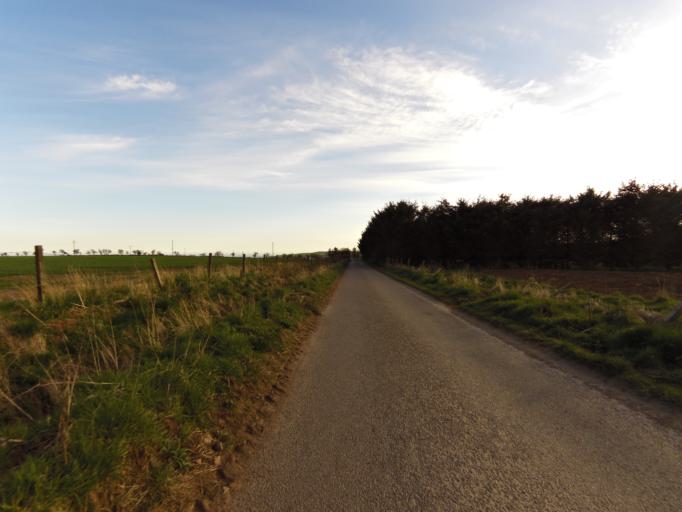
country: GB
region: Scotland
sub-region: Aberdeenshire
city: Stonehaven
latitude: 56.9063
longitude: -2.2143
